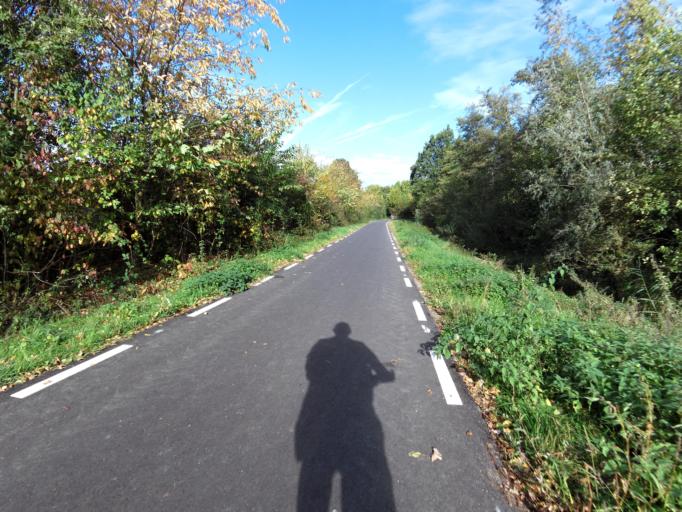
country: NL
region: Limburg
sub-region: Gemeente Onderbanken
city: Schinveld
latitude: 50.9620
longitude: 5.9771
